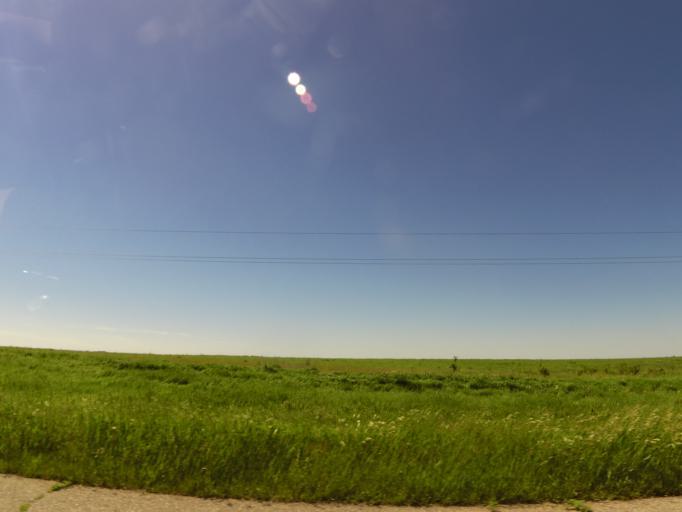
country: US
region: Minnesota
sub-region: Red Lake County
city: Red Lake Falls
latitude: 47.7601
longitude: -96.3111
